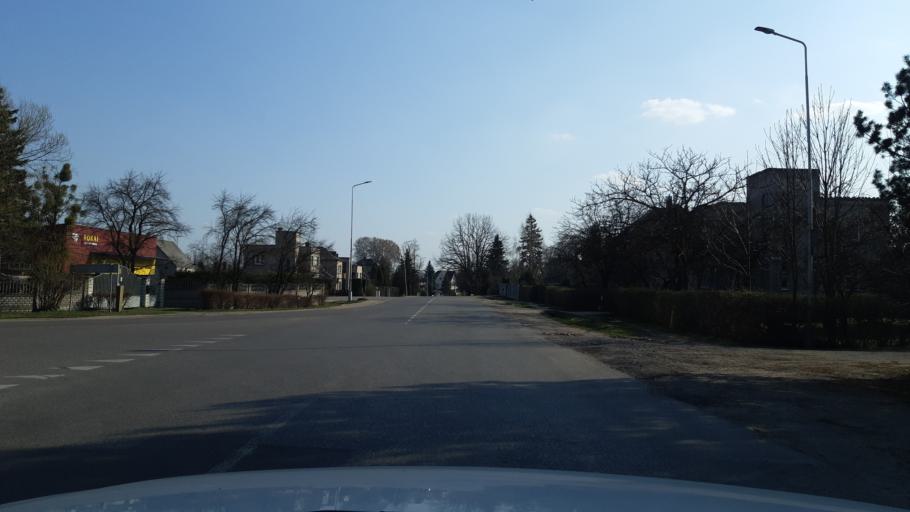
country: LT
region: Kauno apskritis
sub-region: Kaunas
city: Aleksotas
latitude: 54.8394
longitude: 23.9476
